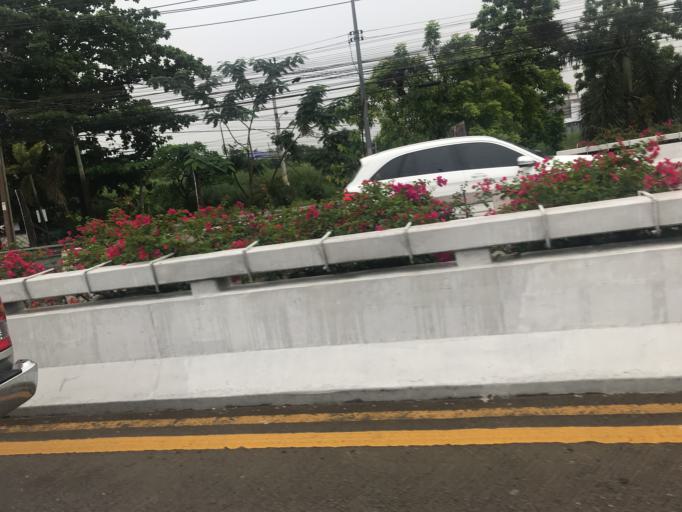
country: TH
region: Bangkok
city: Saphan Sung
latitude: 13.7977
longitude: 100.6968
